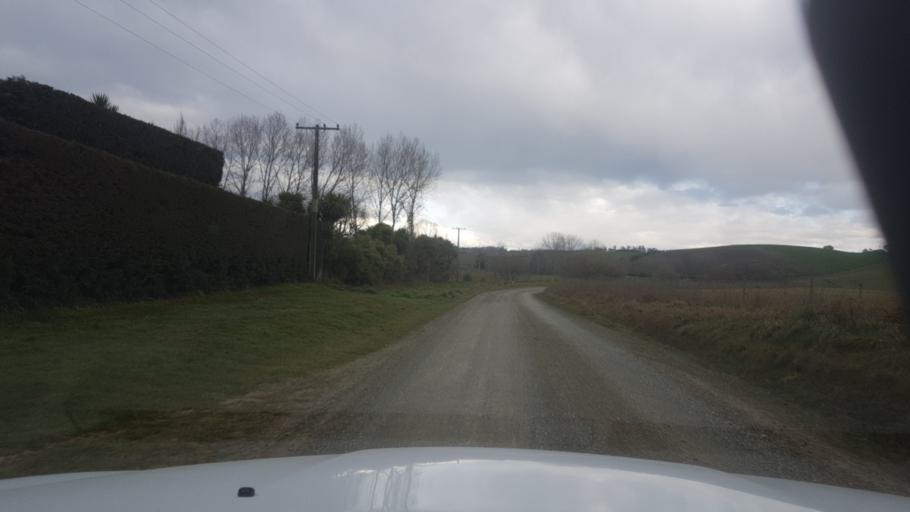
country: NZ
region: Canterbury
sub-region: Timaru District
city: Pleasant Point
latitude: -44.3399
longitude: 171.1710
